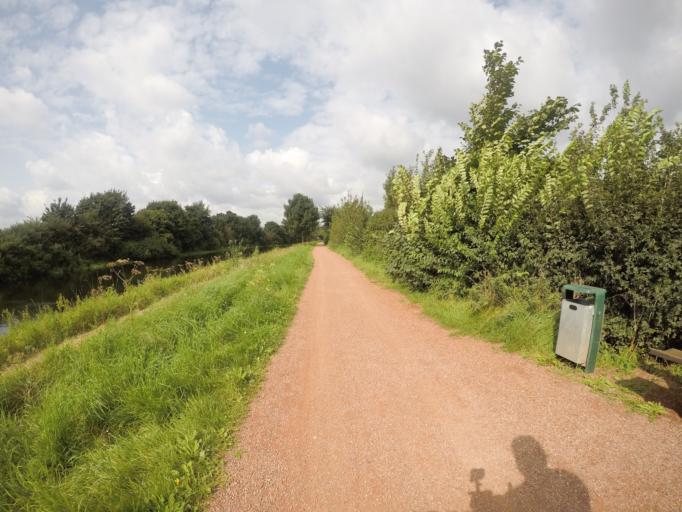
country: DE
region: North Rhine-Westphalia
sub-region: Regierungsbezirk Dusseldorf
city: Bocholt
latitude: 51.8443
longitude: 6.5633
